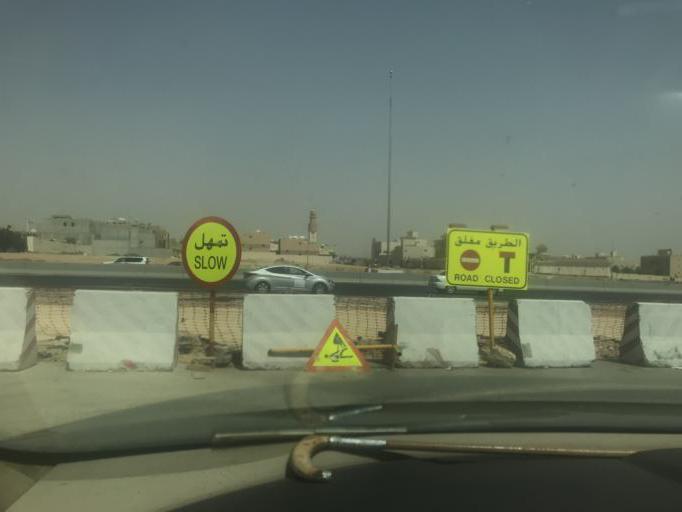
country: SA
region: Ar Riyad
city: Riyadh
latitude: 24.8207
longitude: 46.6010
